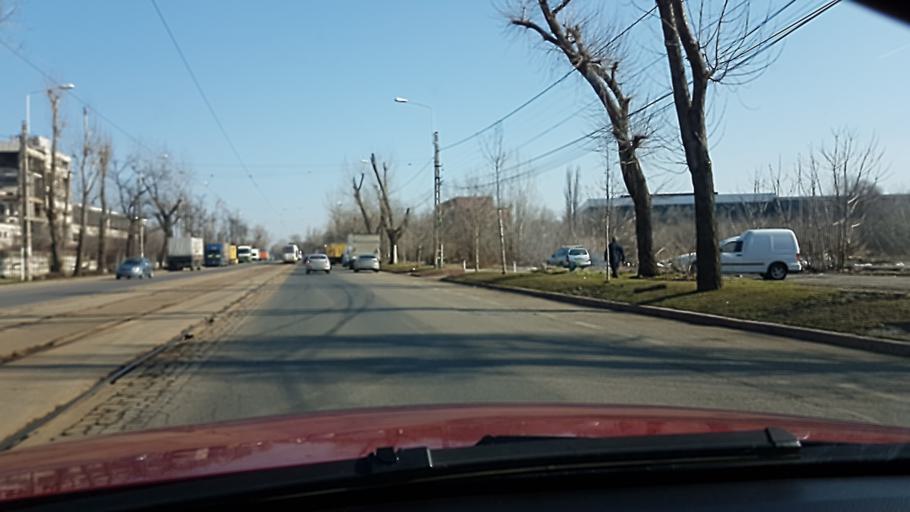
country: RO
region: Ilfov
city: Dobroesti
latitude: 44.4360
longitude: 26.1744
